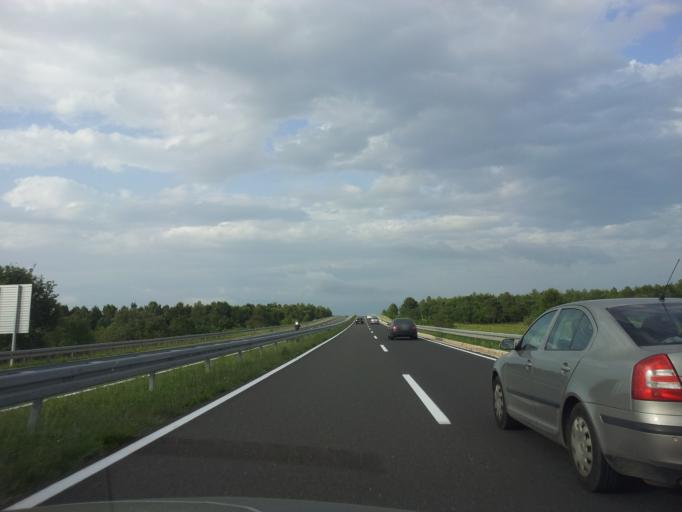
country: HR
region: Zadarska
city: Galovac
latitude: 44.0868
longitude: 15.3585
